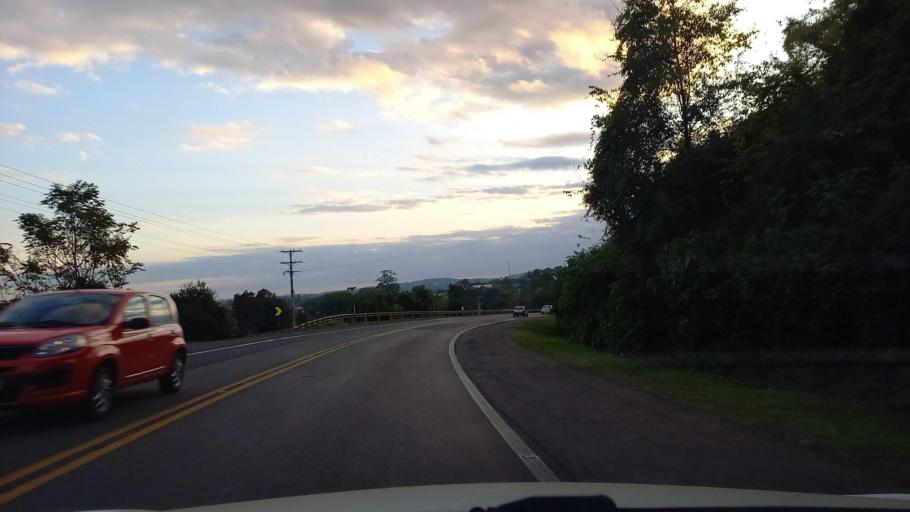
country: BR
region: Rio Grande do Sul
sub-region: Santa Cruz Do Sul
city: Santa Cruz do Sul
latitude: -29.6848
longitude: -52.4384
